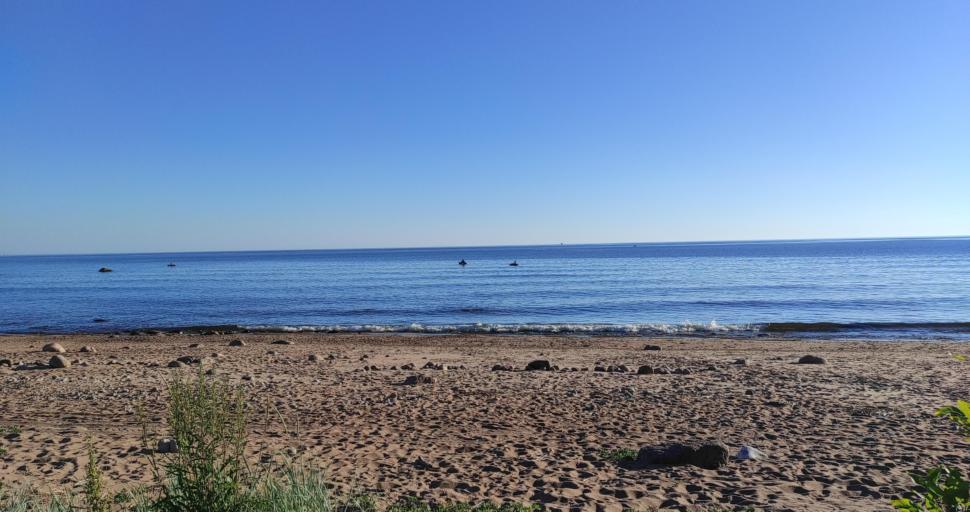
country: RU
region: Leningrad
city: Sosnovyy Bor
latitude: 60.1633
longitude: 29.1420
